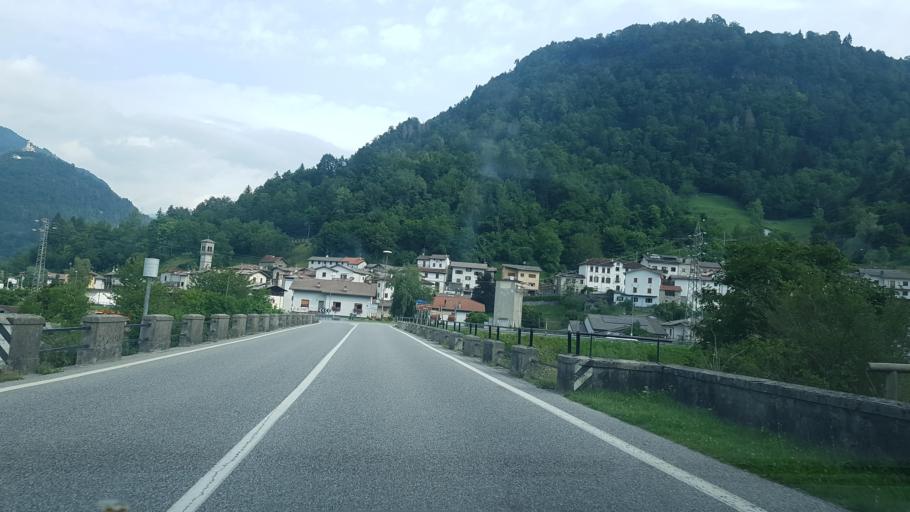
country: IT
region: Friuli Venezia Giulia
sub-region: Provincia di Udine
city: Zuglio
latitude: 46.4562
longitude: 13.0361
